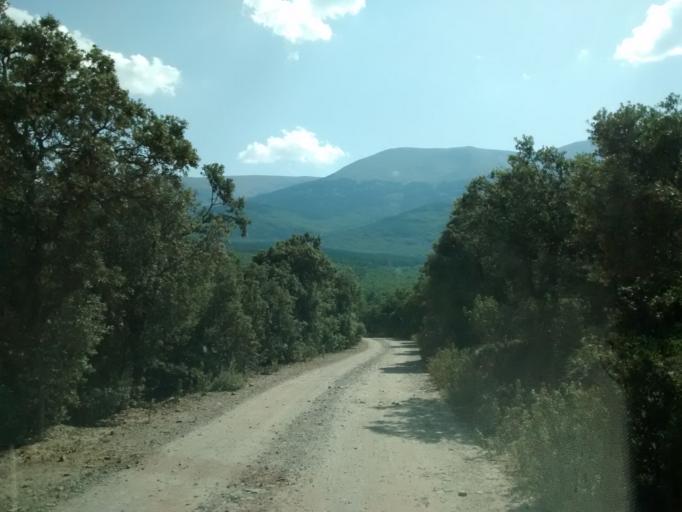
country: ES
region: Aragon
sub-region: Provincia de Zaragoza
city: Lituenigo
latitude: 41.8158
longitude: -1.7901
